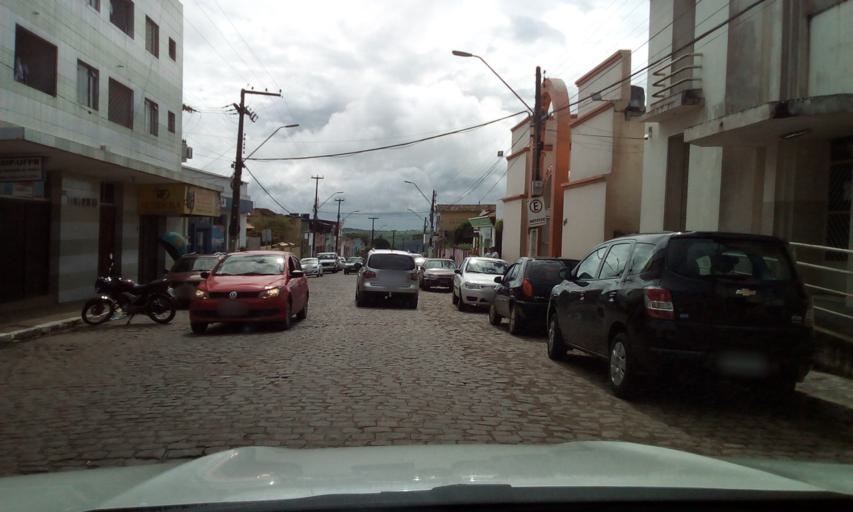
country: BR
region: Paraiba
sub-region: Areia
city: Areia
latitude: -6.9680
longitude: -35.7058
